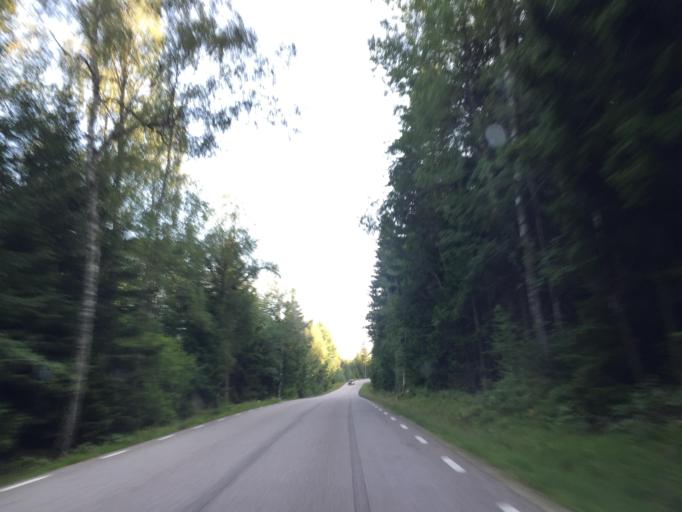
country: SE
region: Vaestra Goetaland
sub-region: Lilla Edets Kommun
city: Lilla Edet
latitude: 58.1374
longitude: 12.0091
